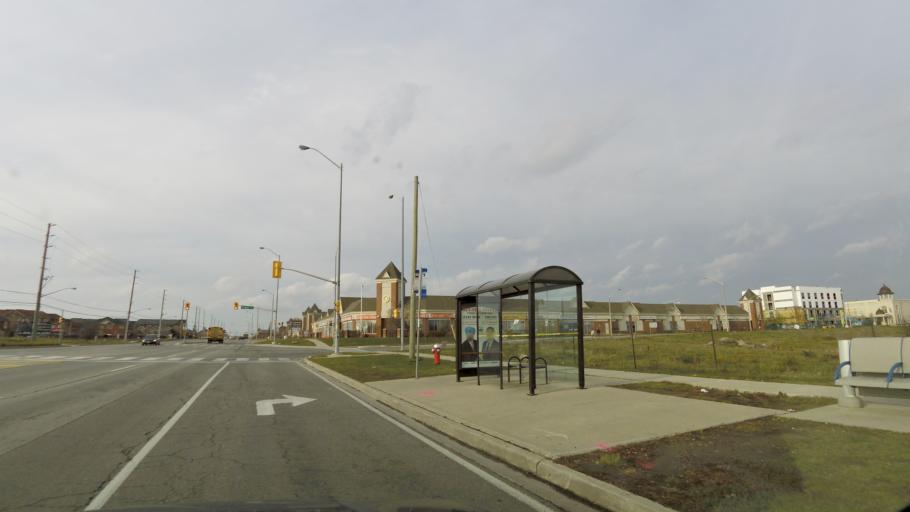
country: CA
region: Ontario
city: Brampton
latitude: 43.7692
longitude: -79.6591
